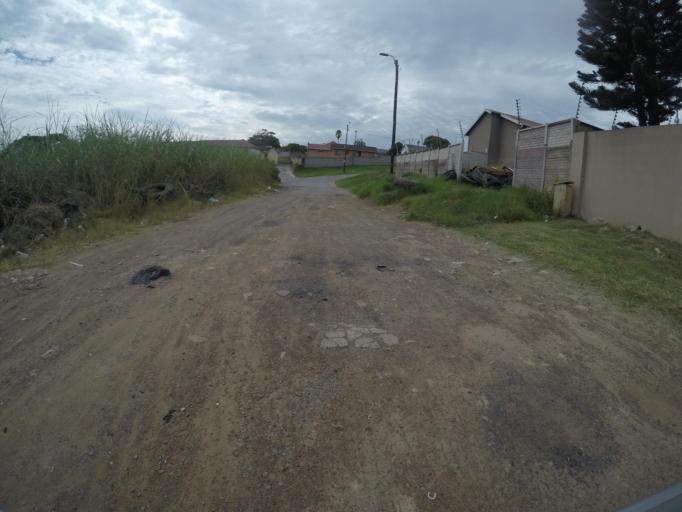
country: ZA
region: Eastern Cape
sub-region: Buffalo City Metropolitan Municipality
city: East London
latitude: -32.9932
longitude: 27.8647
